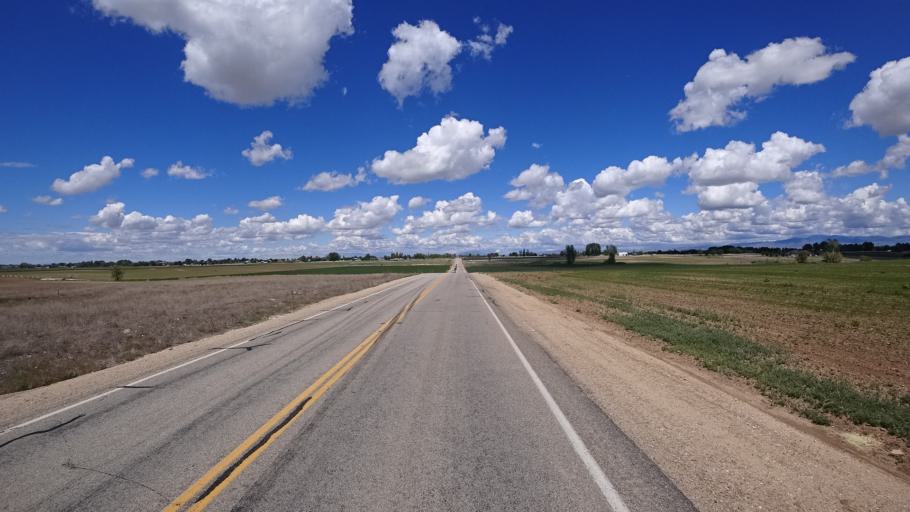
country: US
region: Idaho
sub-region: Ada County
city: Meridian
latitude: 43.5672
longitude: -116.4338
